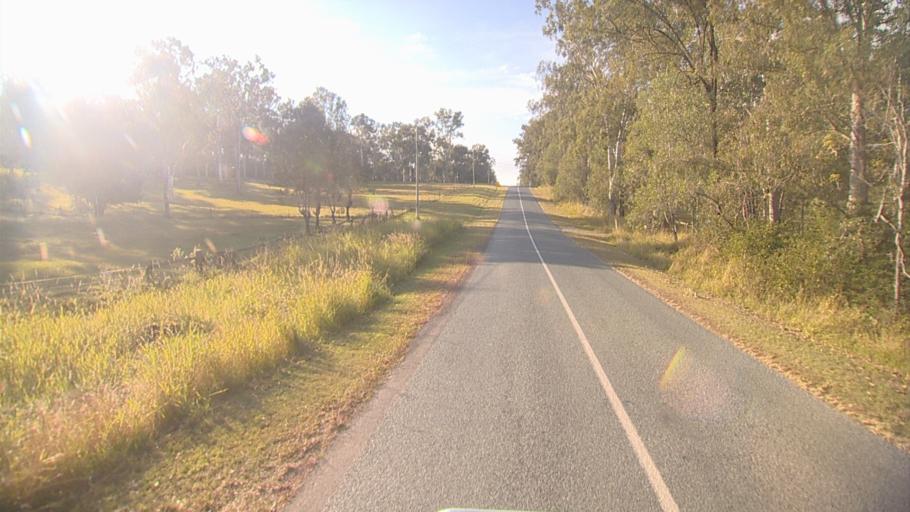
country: AU
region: Queensland
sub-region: Gold Coast
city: Ormeau Hills
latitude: -27.8365
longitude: 153.1688
